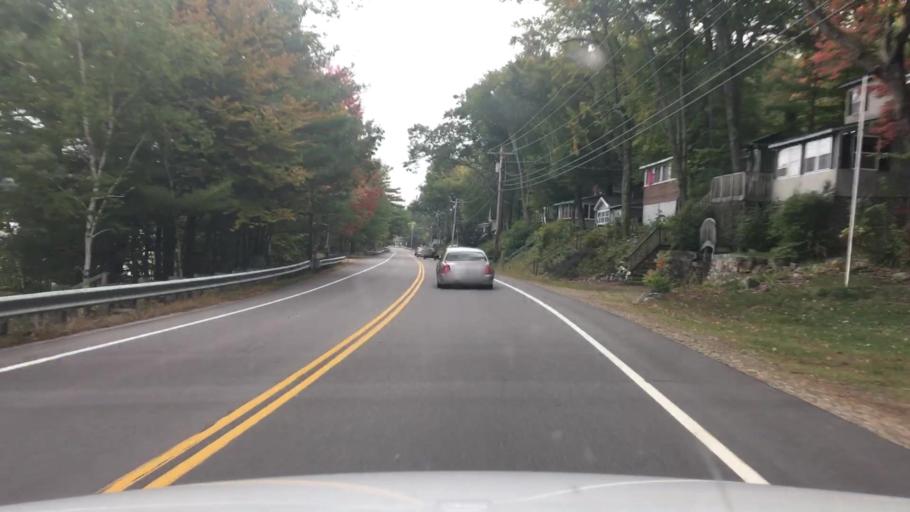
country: US
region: New Hampshire
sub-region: Strafford County
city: New Durham
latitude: 43.4799
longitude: -71.2416
